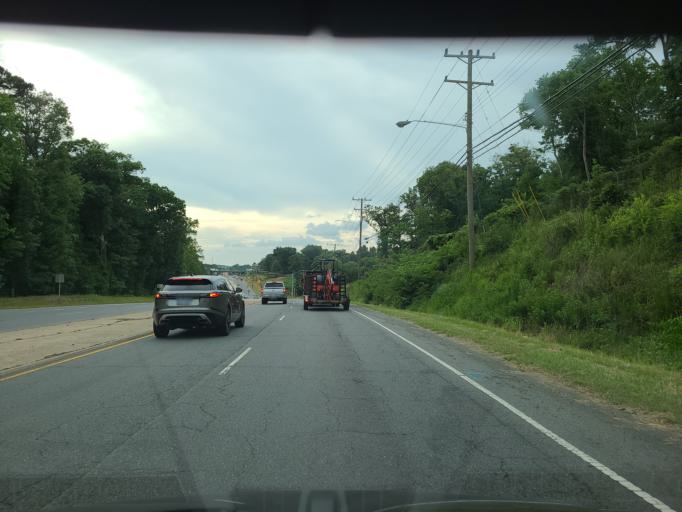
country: US
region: North Carolina
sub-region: Gaston County
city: Belmont
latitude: 35.2379
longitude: -80.9601
